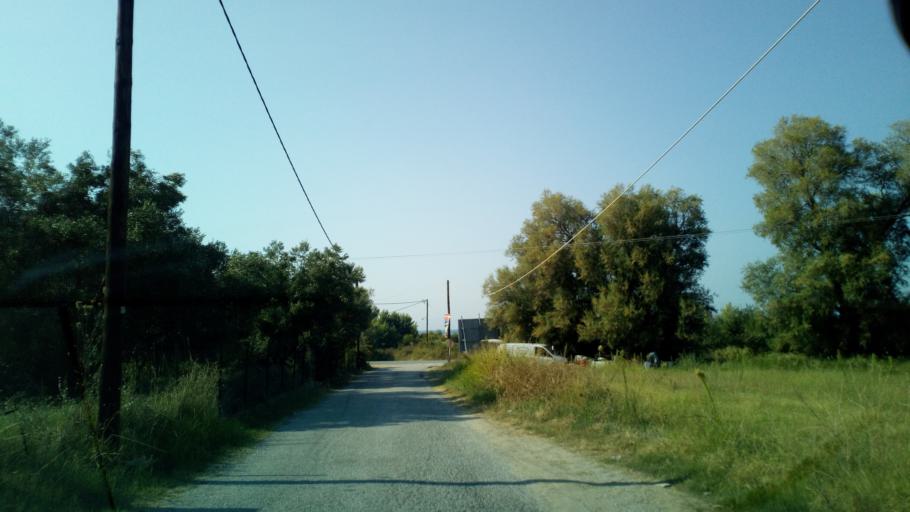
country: GR
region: Central Macedonia
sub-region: Nomos Chalkidikis
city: Pefkochori
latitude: 39.9770
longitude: 23.6513
